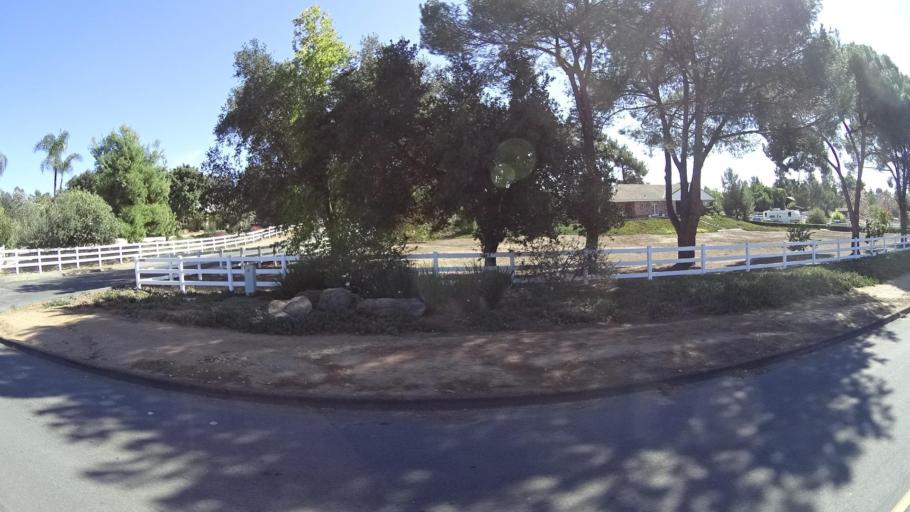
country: US
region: California
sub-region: San Diego County
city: Harbison Canyon
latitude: 32.8681
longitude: -116.8603
